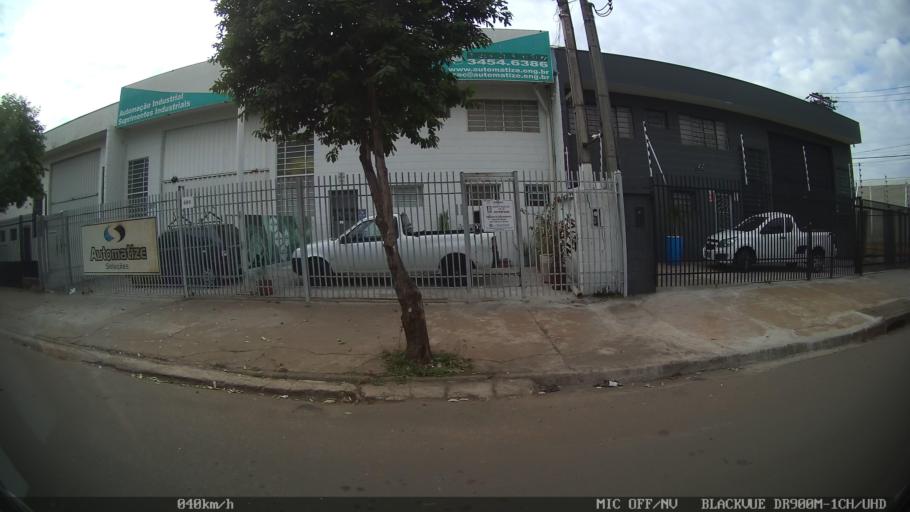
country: BR
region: Sao Paulo
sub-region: Santa Barbara D'Oeste
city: Santa Barbara d'Oeste
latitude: -22.7588
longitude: -47.3861
